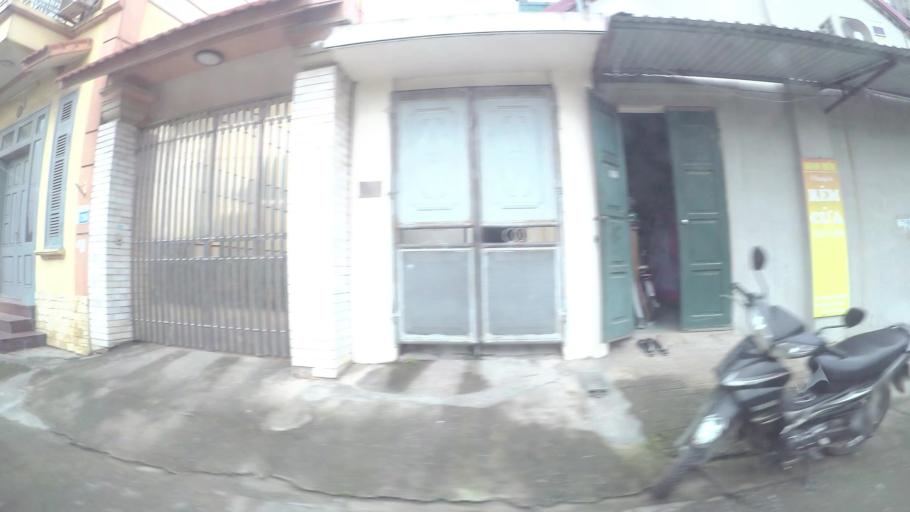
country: VN
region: Ha Noi
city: Van Dien
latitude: 20.9671
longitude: 105.8748
